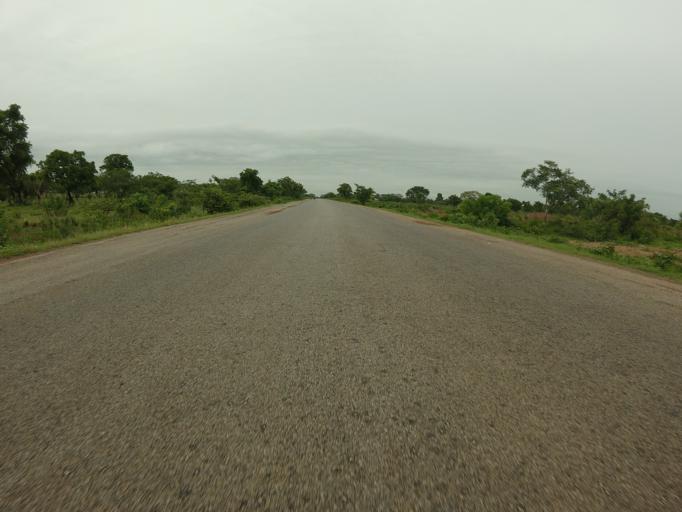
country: GH
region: Northern
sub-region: Yendi
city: Yendi
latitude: 9.5161
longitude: -0.0288
